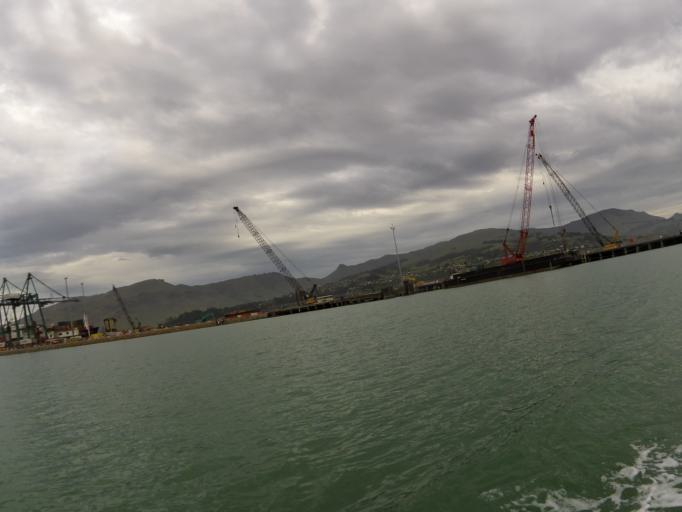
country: NZ
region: Canterbury
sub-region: Christchurch City
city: Christchurch
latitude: -43.6082
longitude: 172.7190
